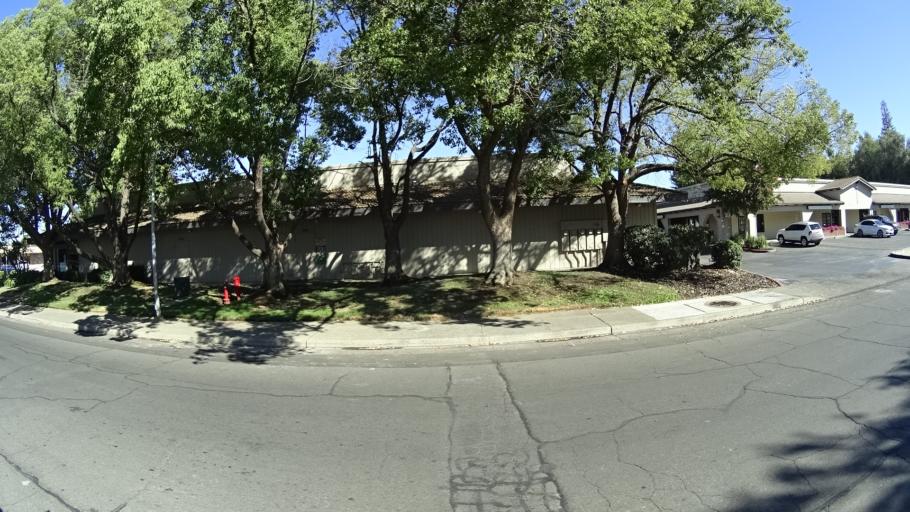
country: US
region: California
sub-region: Sacramento County
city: Elk Grove
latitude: 38.4057
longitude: -121.3710
